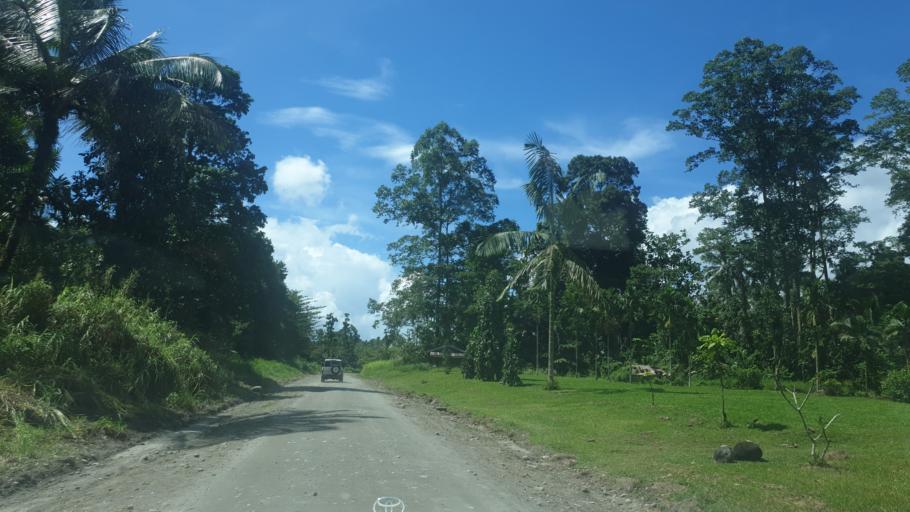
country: PG
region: Bougainville
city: Panguna
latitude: -6.6601
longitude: 155.4442
